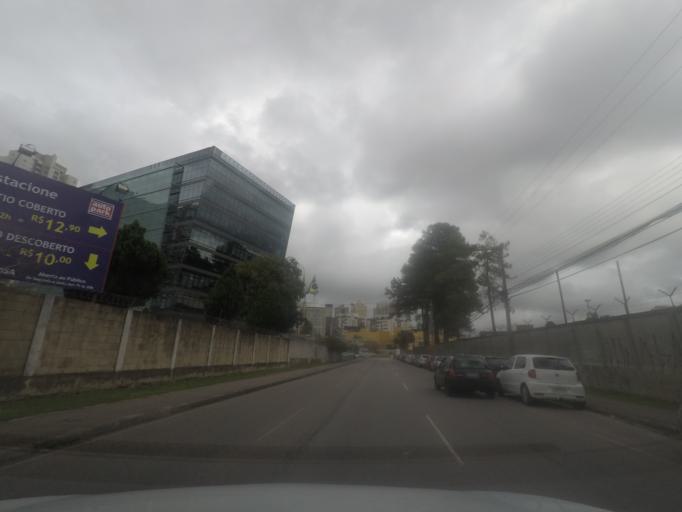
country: BR
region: Parana
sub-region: Curitiba
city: Curitiba
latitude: -25.4385
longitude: -49.2418
